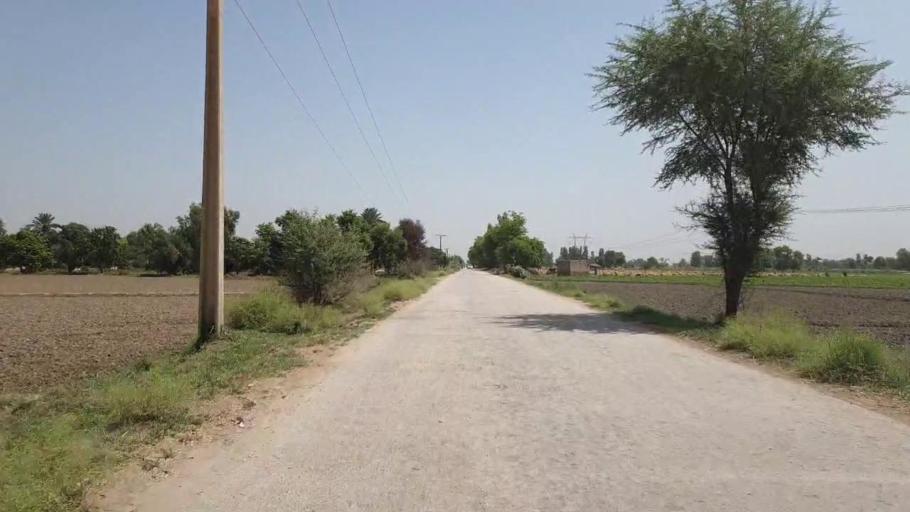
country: PK
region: Sindh
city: Adilpur
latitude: 27.8318
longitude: 69.2558
